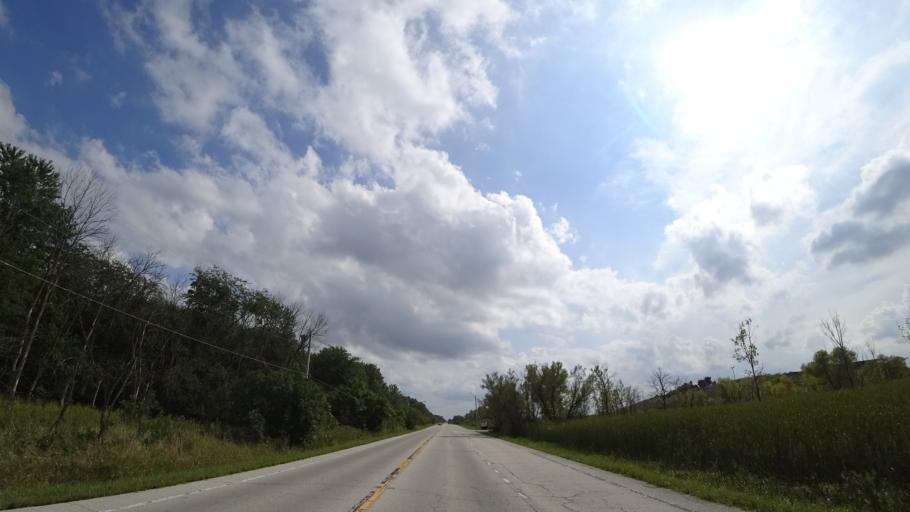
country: US
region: Illinois
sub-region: Cook County
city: Tinley Park
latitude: 41.5469
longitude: -87.7711
